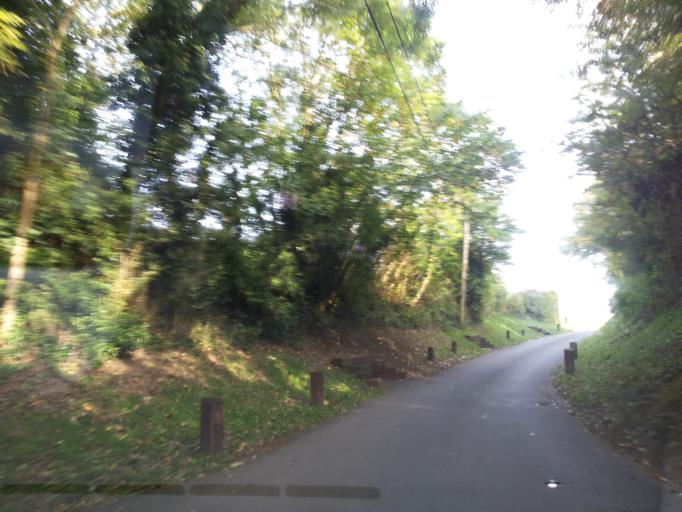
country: GB
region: England
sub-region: Worcestershire
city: Stourport-on-Severn
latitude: 52.3461
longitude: -2.2980
